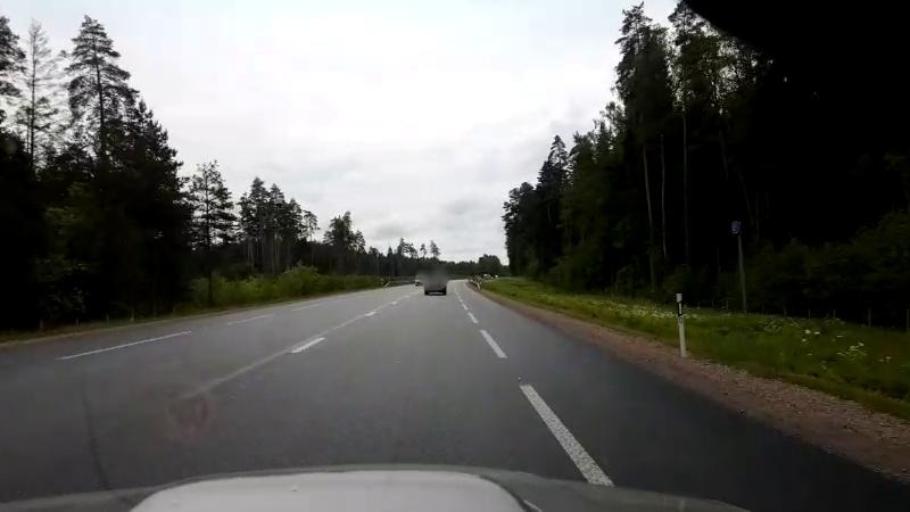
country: LV
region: Kekava
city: Kekava
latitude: 56.7244
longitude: 24.2536
